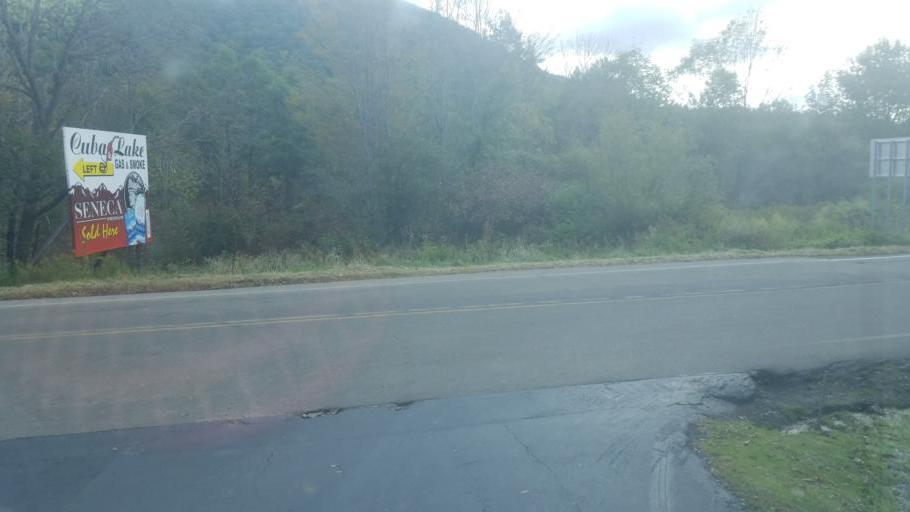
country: US
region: New York
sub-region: Allegany County
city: Cuba
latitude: 42.2244
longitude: -78.3115
